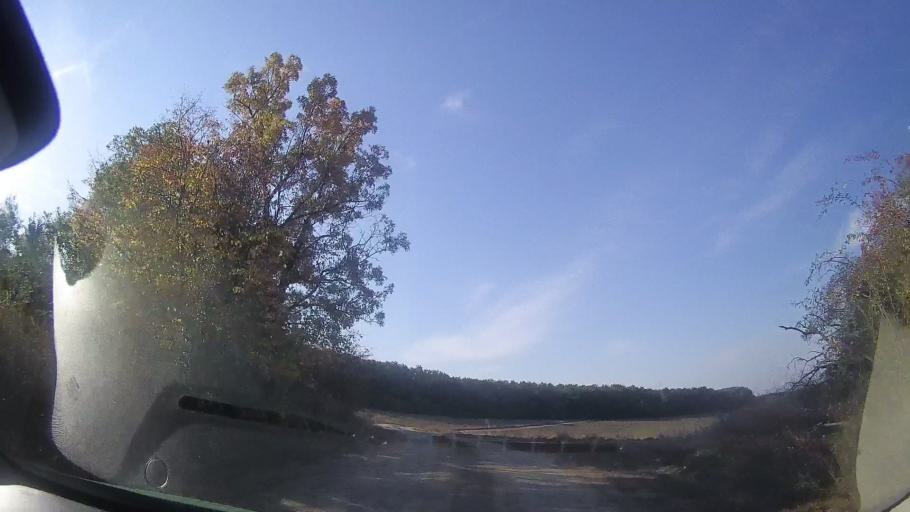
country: RO
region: Timis
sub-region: Comuna Bogda
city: Bogda
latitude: 45.9090
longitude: 21.5846
